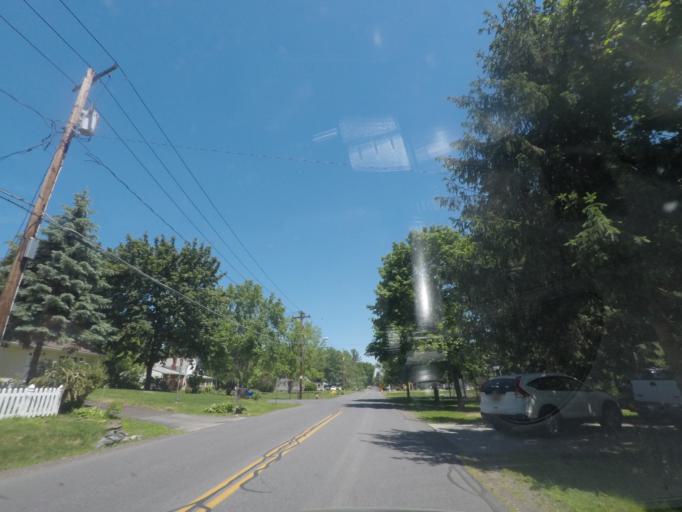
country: US
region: New York
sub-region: Saratoga County
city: Stillwater
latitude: 42.9378
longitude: -73.6617
